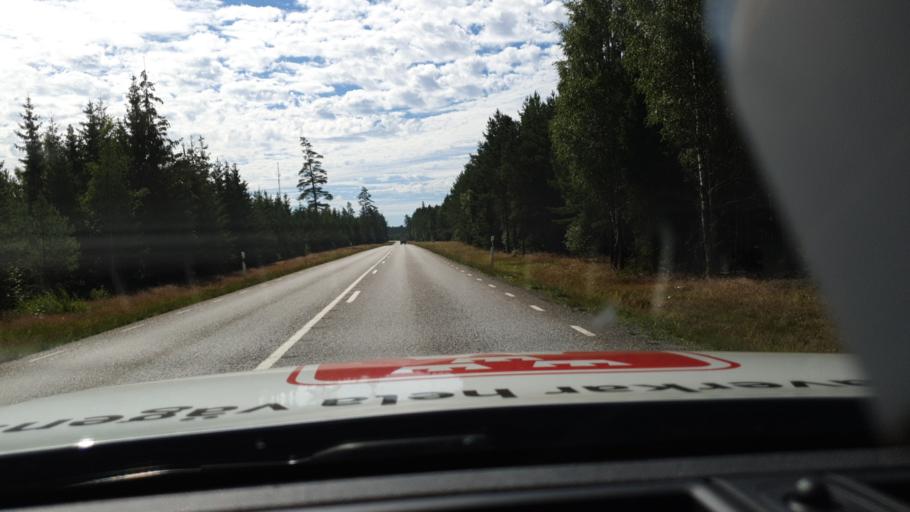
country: SE
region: Joenkoeping
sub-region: Vaggeryds Kommun
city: Vaggeryd
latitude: 57.5987
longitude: 14.2204
